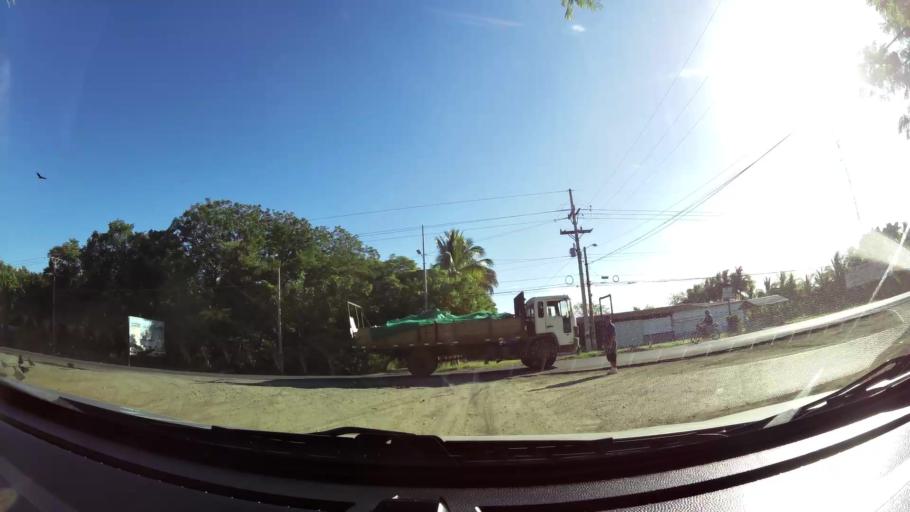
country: CR
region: Guanacaste
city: Belen
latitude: 10.4874
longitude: -85.5682
